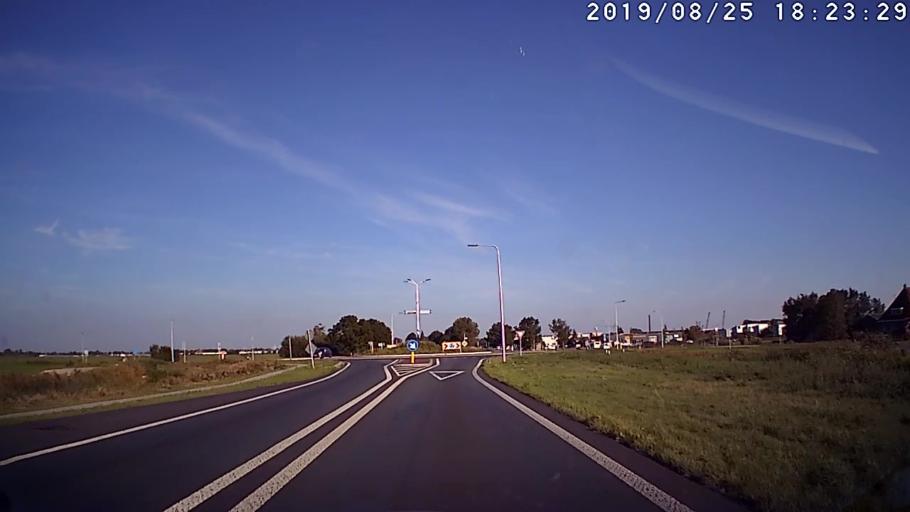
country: NL
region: Friesland
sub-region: Gemeente Lemsterland
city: Lemmer
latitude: 52.8560
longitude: 5.6655
